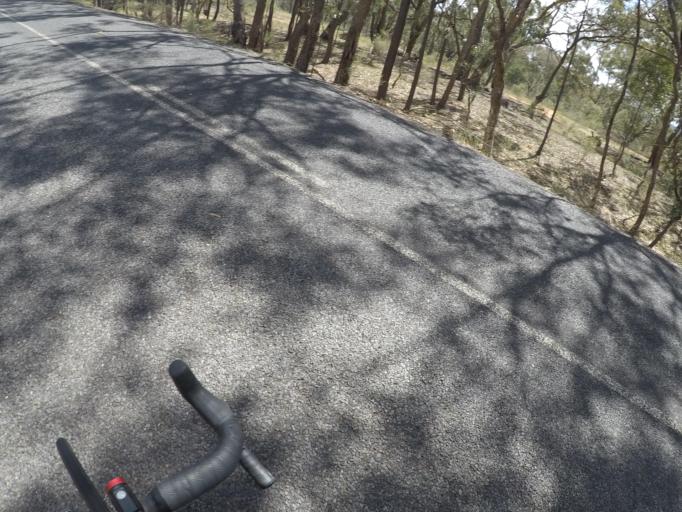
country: AU
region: New South Wales
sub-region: Blayney
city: Blayney
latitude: -33.5814
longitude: 149.3926
